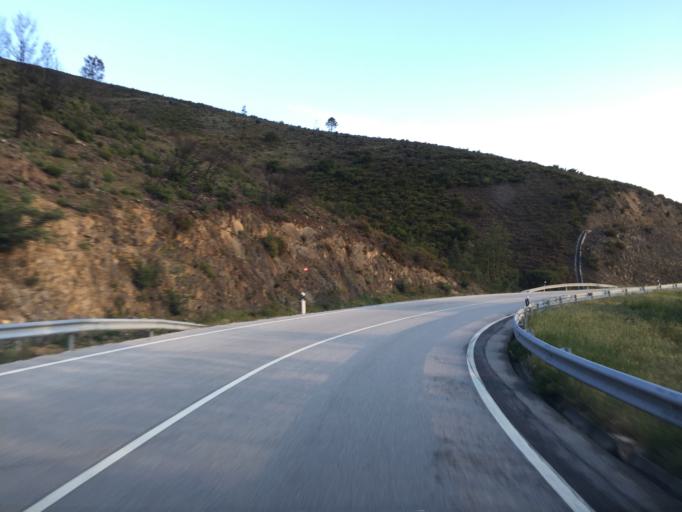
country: PT
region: Coimbra
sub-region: Pampilhosa da Serra
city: Pampilhosa da Serra
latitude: 40.0942
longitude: -7.9887
